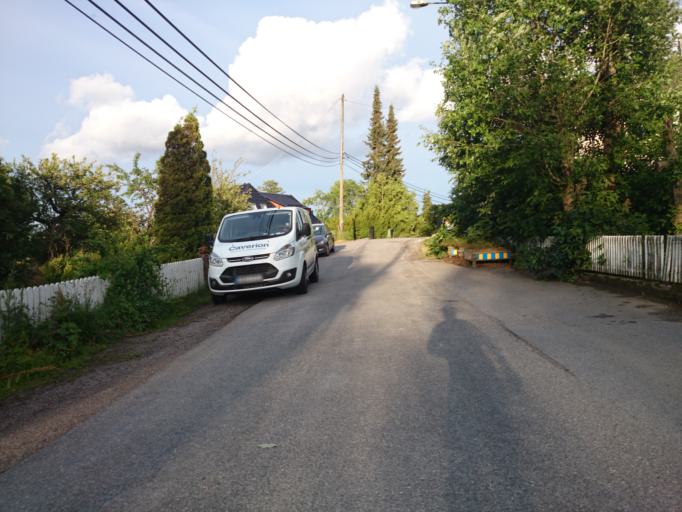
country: SE
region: Stockholm
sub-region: Huddinge Kommun
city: Segeltorp
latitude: 59.2712
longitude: 17.9569
